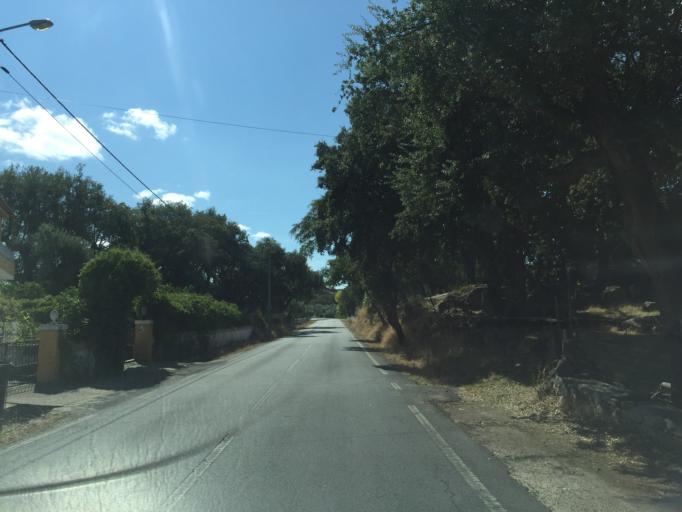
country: PT
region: Portalegre
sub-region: Marvao
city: Marvao
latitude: 39.4384
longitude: -7.3652
